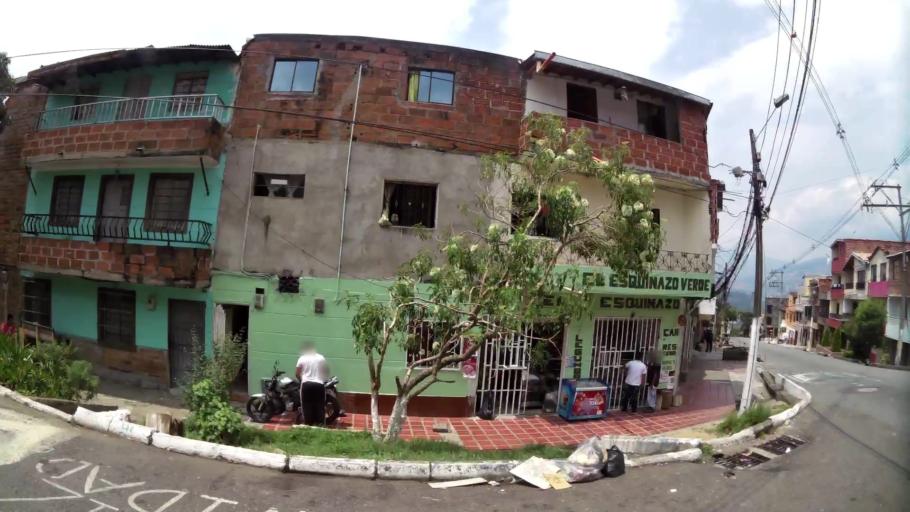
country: CO
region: Antioquia
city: Medellin
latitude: 6.2631
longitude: -75.5505
